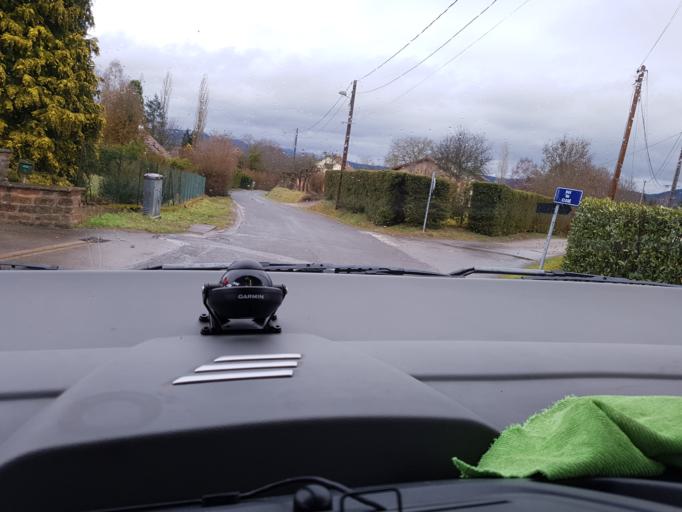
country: FR
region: Lorraine
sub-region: Departement des Vosges
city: Saint-Michel-sur-Meurthe
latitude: 48.3118
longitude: 6.8849
